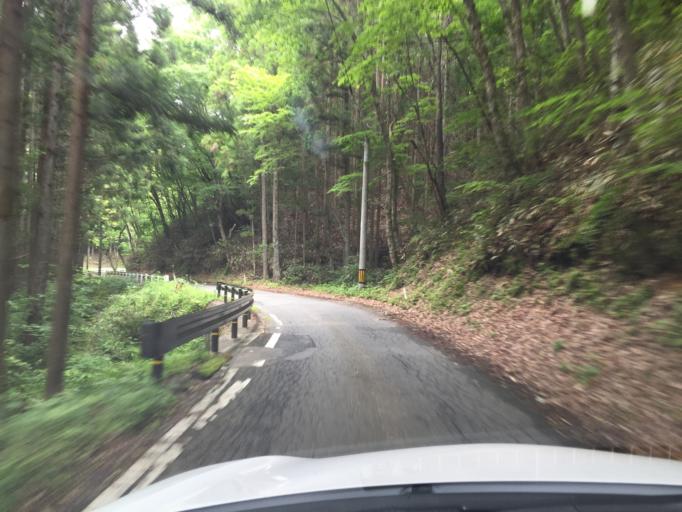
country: JP
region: Fukushima
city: Iwaki
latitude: 37.2046
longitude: 140.7222
